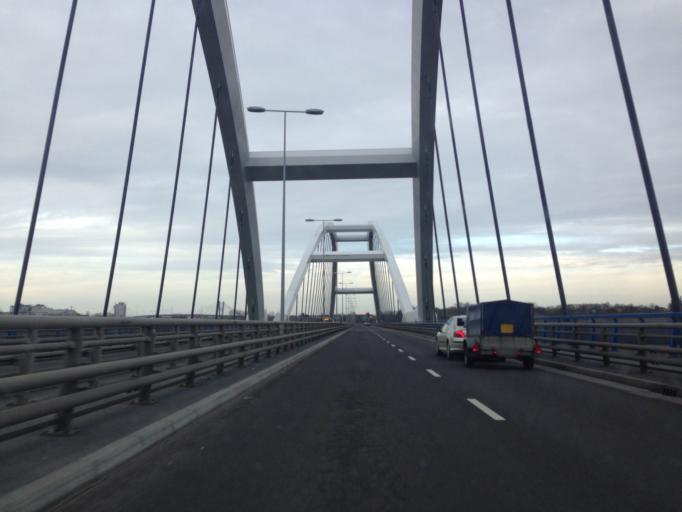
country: PL
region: Kujawsko-Pomorskie
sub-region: Torun
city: Torun
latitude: 53.0137
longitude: 18.6553
